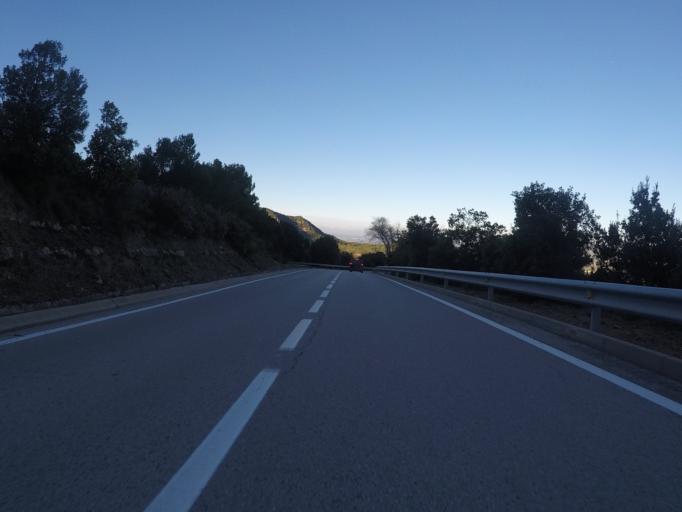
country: ES
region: Catalonia
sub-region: Provincia de Barcelona
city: Monistrol de Montserrat
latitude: 41.6125
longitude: 1.8232
